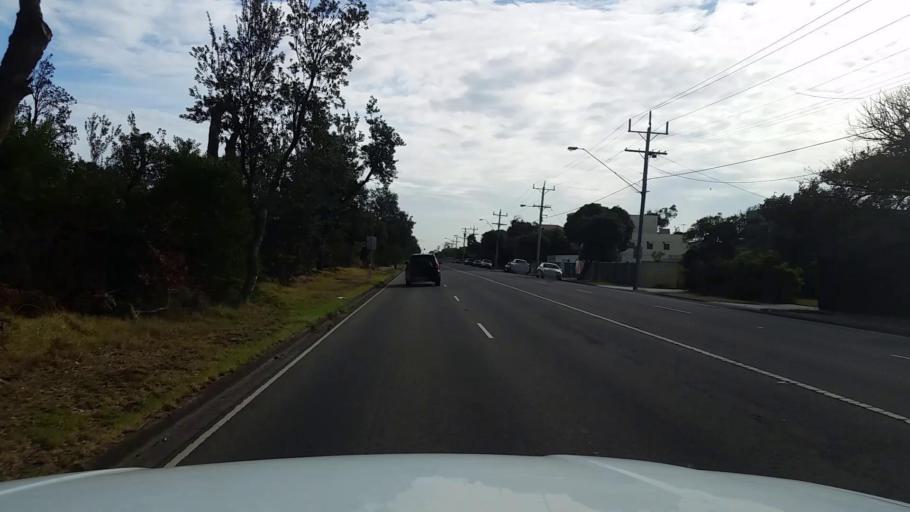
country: AU
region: Victoria
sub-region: Frankston
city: Seaford
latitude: -38.1141
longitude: 145.1256
